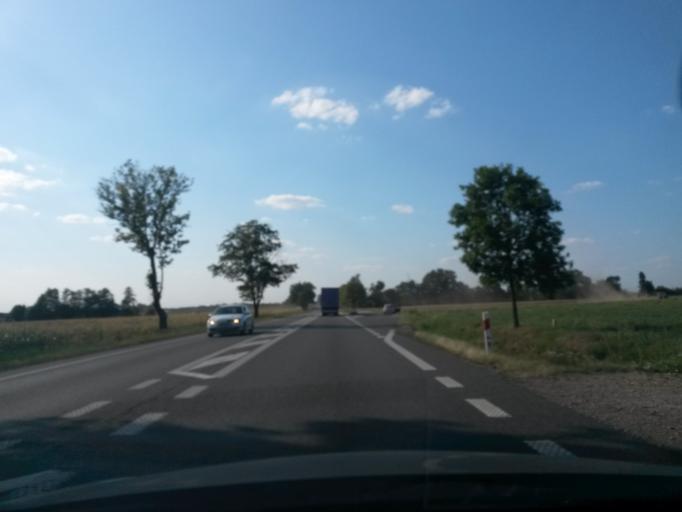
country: PL
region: Masovian Voivodeship
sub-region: Powiat sierpecki
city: Rosciszewo
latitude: 52.8319
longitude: 19.7493
